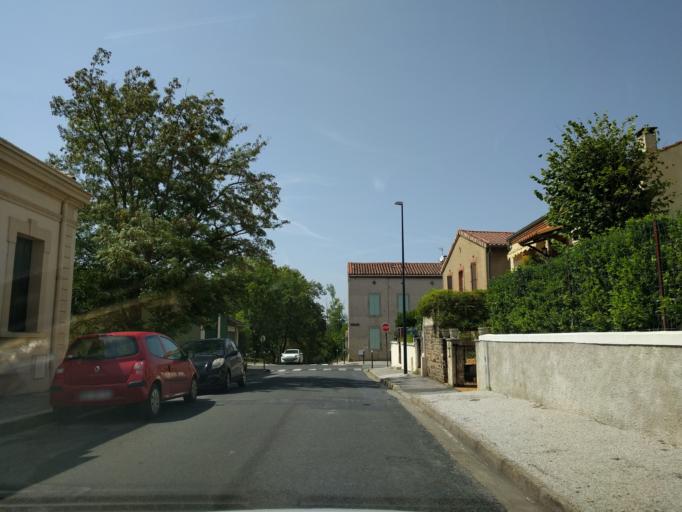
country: FR
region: Midi-Pyrenees
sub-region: Departement du Tarn
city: Castres
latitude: 43.5967
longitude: 2.2425
